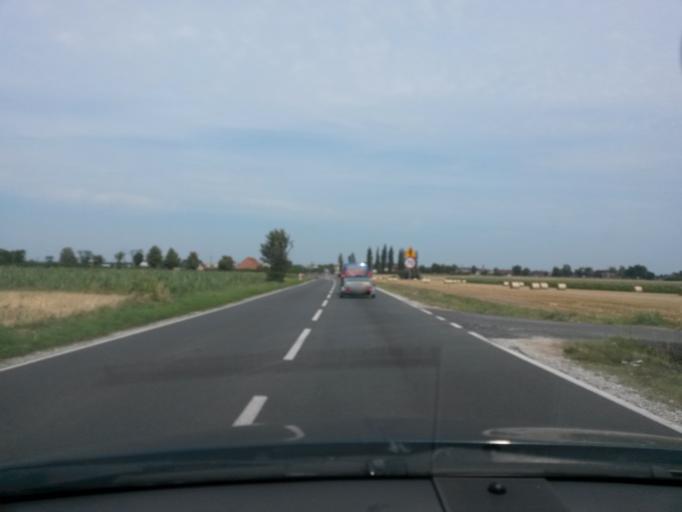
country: PL
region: Greater Poland Voivodeship
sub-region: Powiat gostynski
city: Krobia
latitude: 51.7540
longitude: 16.9647
